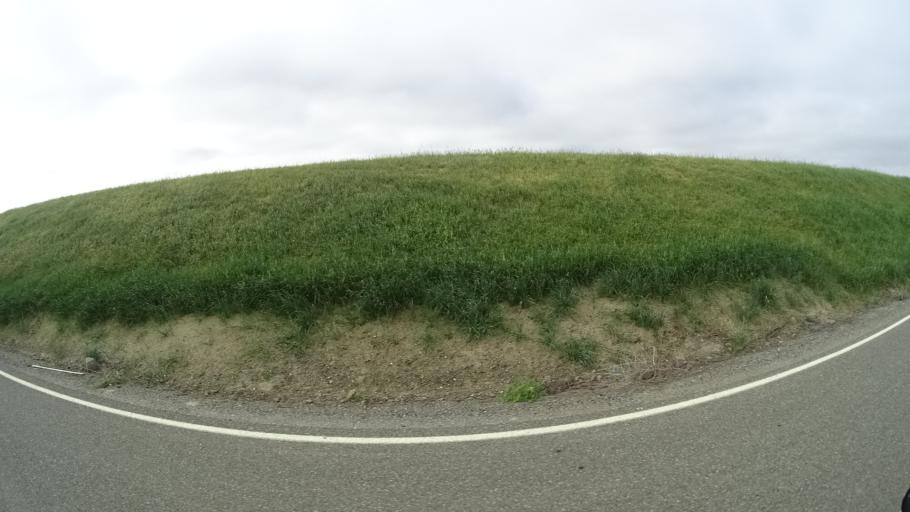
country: US
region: California
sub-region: Colusa County
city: Colusa
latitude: 39.3891
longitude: -121.9930
